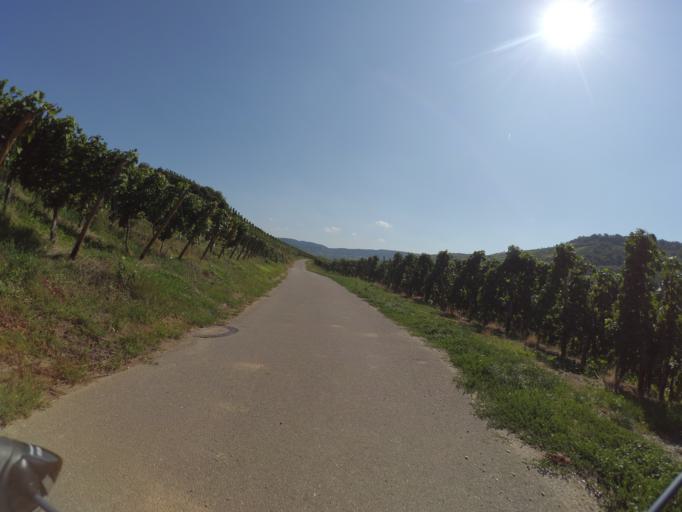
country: DE
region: Rheinland-Pfalz
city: Neumagen-Dhron
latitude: 49.8457
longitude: 6.8954
